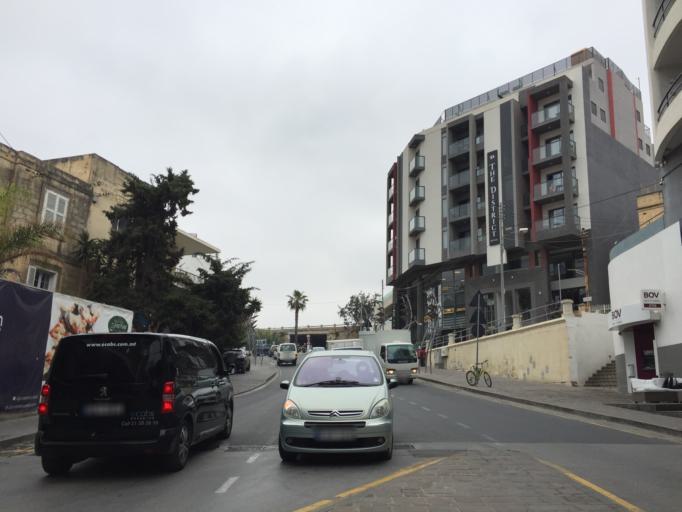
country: MT
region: Saint Julian
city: San Giljan
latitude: 35.9235
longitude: 14.4873
